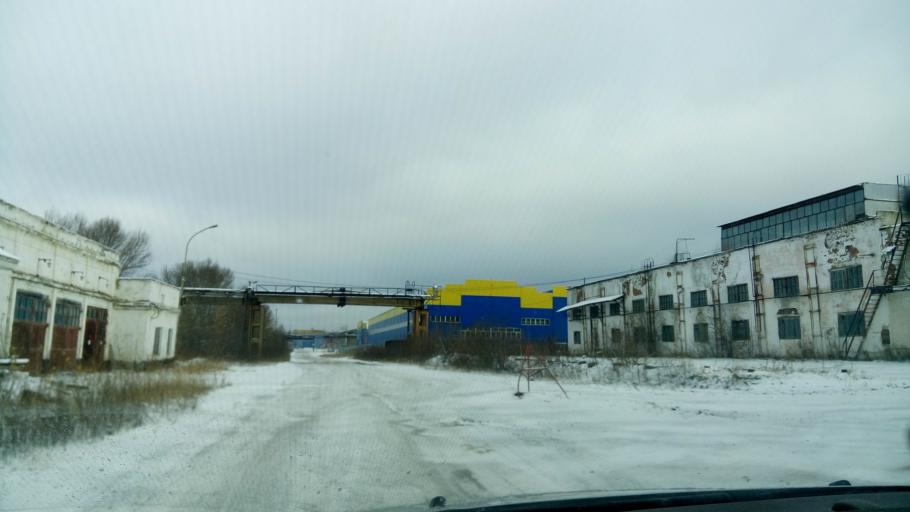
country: RU
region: Sverdlovsk
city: Polevskoy
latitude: 56.4682
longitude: 60.1780
